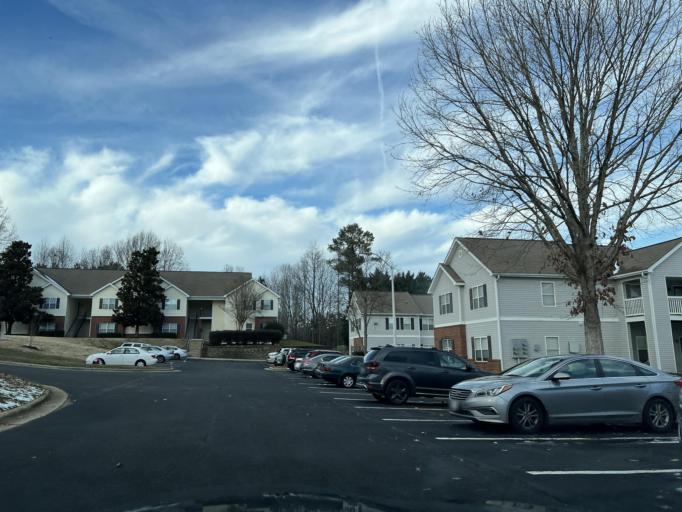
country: US
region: North Carolina
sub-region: Wake County
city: Raleigh
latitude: 35.8729
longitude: -78.5868
